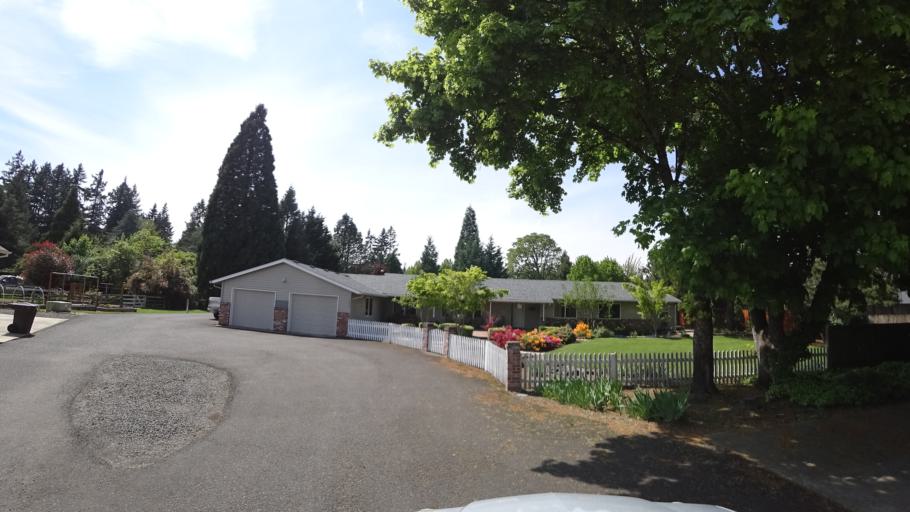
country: US
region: Oregon
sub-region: Washington County
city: Hillsboro
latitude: 45.5110
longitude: -122.9376
